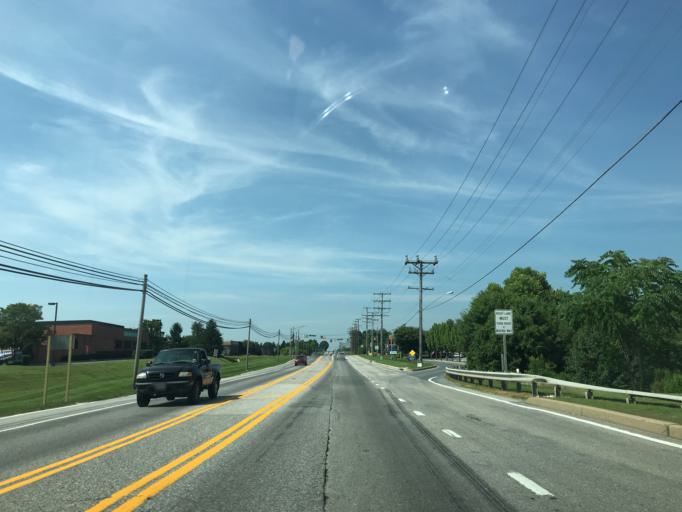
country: US
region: Maryland
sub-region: Carroll County
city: Westminster
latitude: 39.6047
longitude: -76.9984
